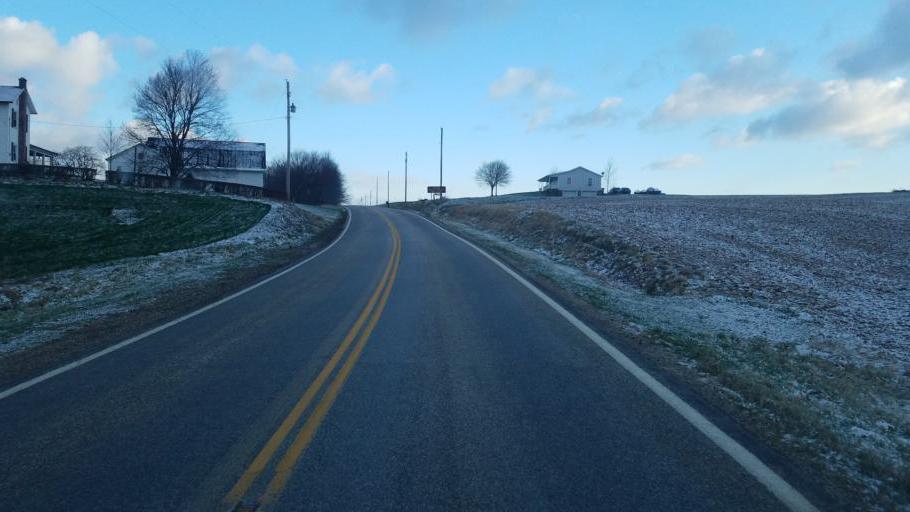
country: US
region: Ohio
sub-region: Ashland County
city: Loudonville
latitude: 40.6763
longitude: -82.1458
